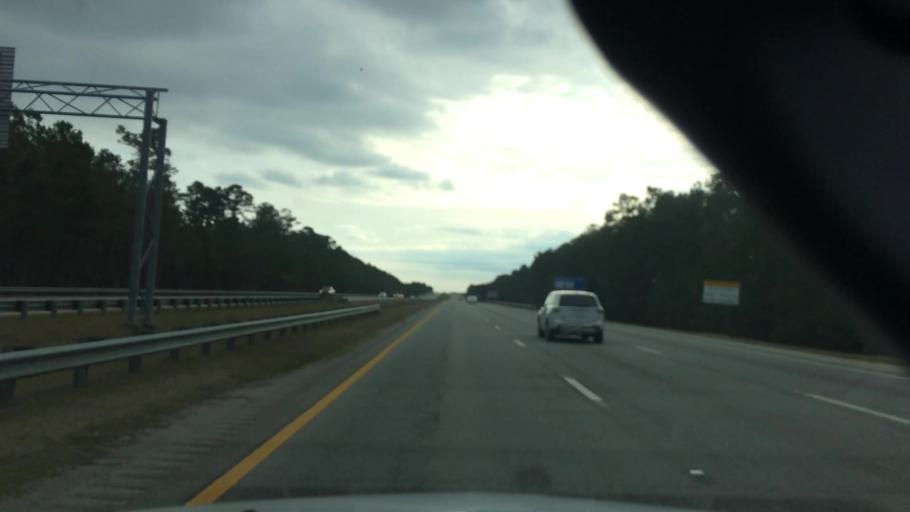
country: US
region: South Carolina
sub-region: Horry County
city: North Myrtle Beach
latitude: 33.8619
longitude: -78.6953
